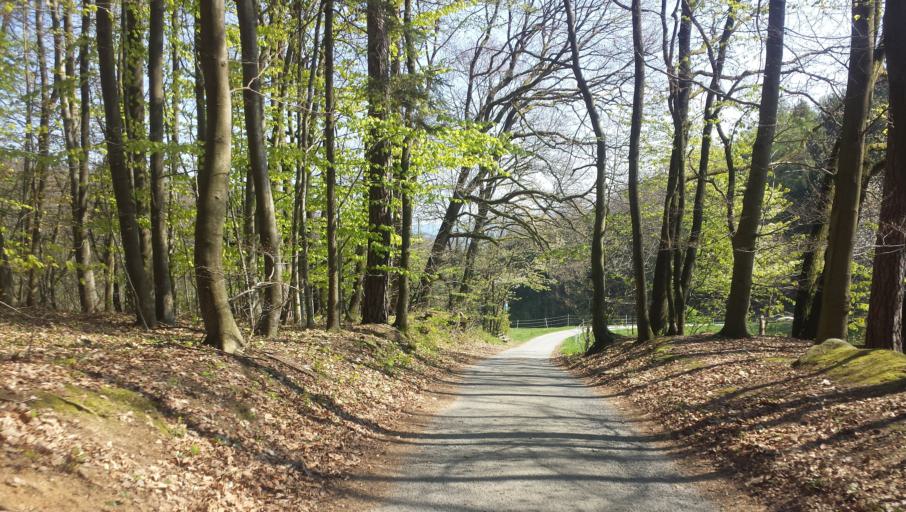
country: DE
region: Hesse
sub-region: Regierungsbezirk Darmstadt
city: Morlenbach
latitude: 49.6274
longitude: 8.7087
